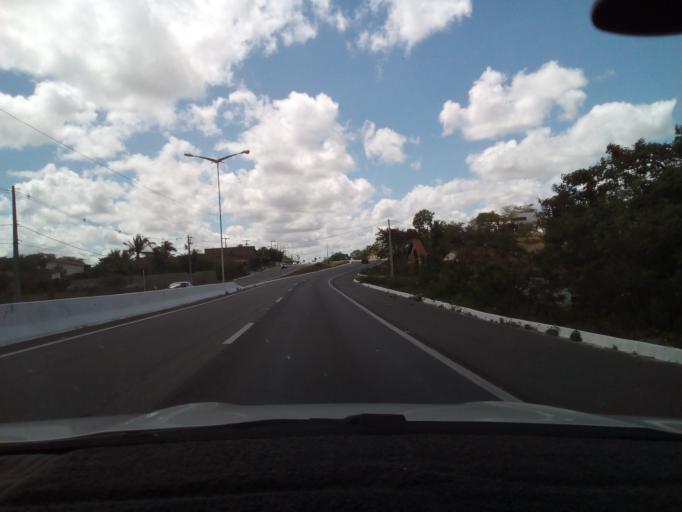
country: BR
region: Paraiba
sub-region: Campina Grande
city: Campina Grande
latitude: -7.2458
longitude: -35.8503
